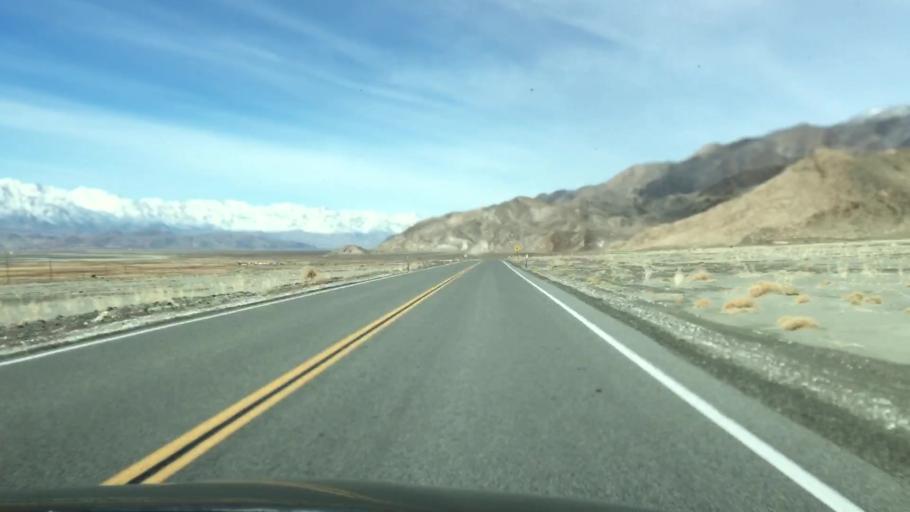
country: US
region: California
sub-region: Inyo County
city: Lone Pine
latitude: 36.5121
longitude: -117.8948
